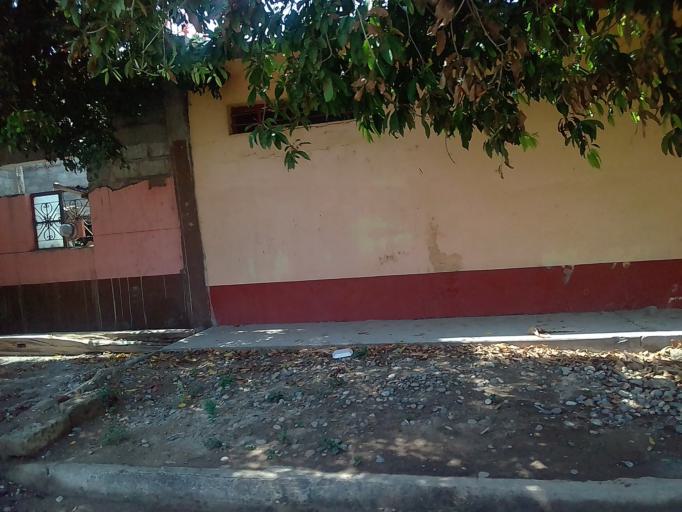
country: MX
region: Oaxaca
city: Union Hidalgo
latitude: 16.4745
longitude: -94.8319
